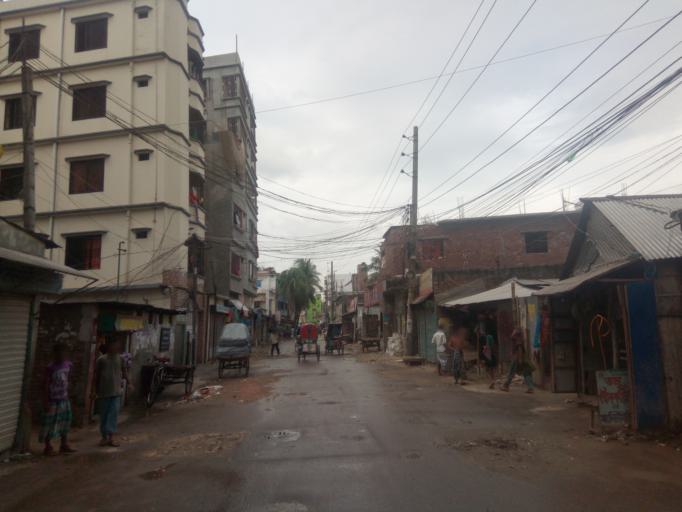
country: BD
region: Dhaka
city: Azimpur
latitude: 23.7092
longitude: 90.3716
